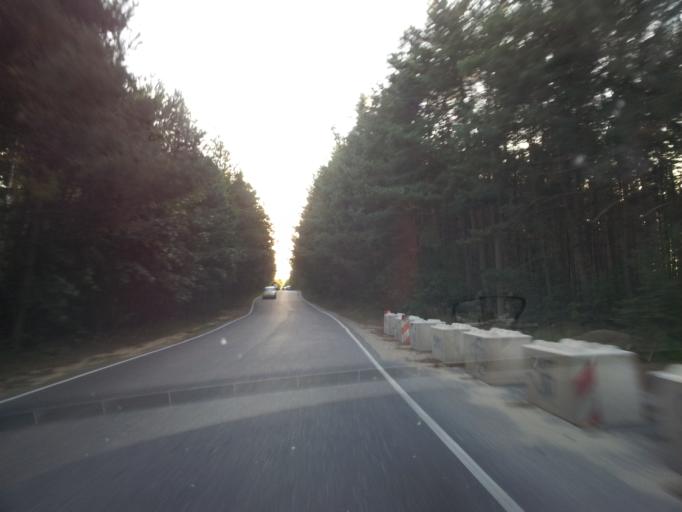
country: DE
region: Saxony
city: Ottendorf-Okrilla
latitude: 51.1969
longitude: 13.8238
